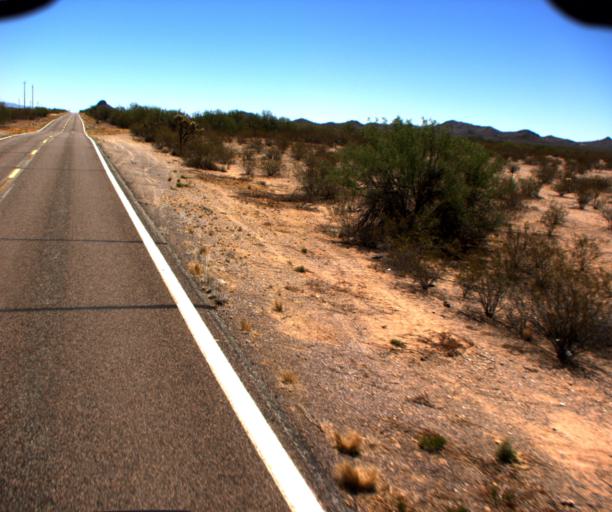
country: US
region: Arizona
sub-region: Pima County
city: Ajo
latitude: 32.2068
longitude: -112.5799
